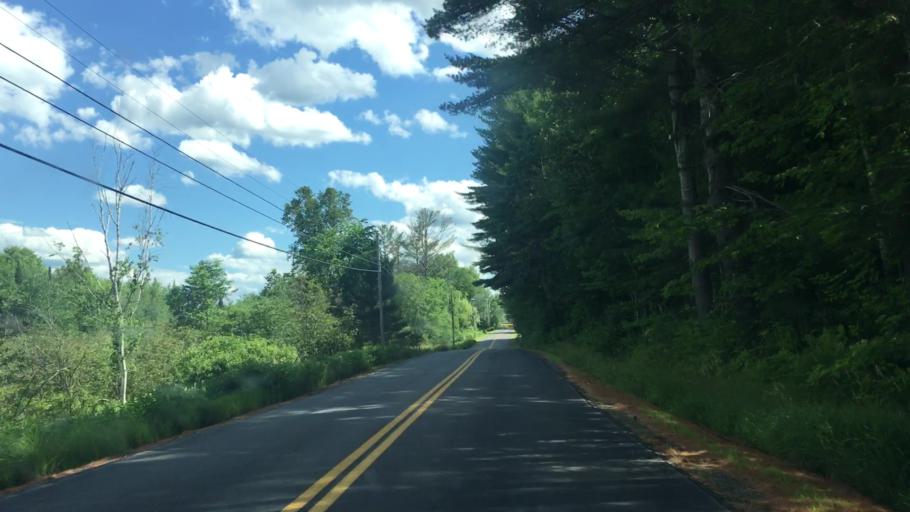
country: US
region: Maine
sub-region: Franklin County
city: Farmington
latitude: 44.6794
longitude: -70.1318
